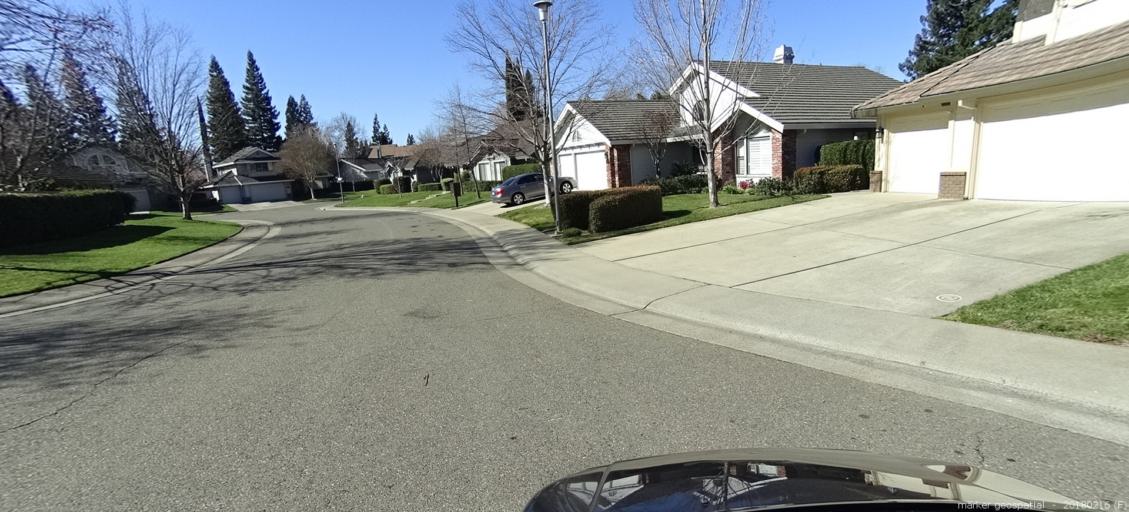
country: US
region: California
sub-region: Sacramento County
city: Gold River
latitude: 38.6252
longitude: -121.2329
